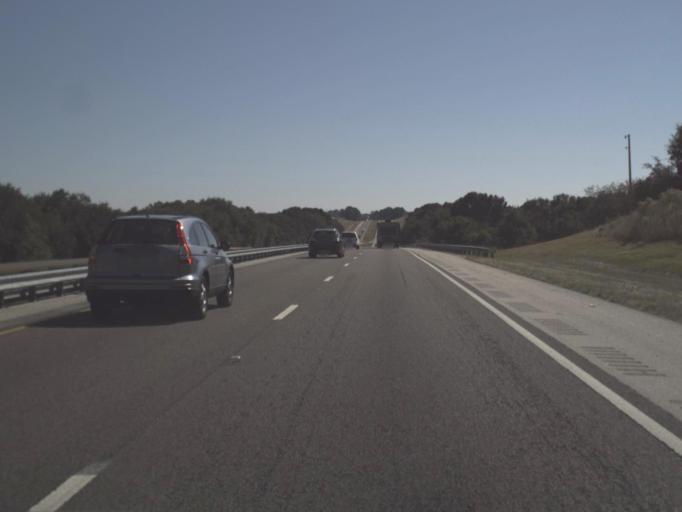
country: US
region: Florida
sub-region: Lake County
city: Montverde
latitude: 28.5701
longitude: -81.6939
